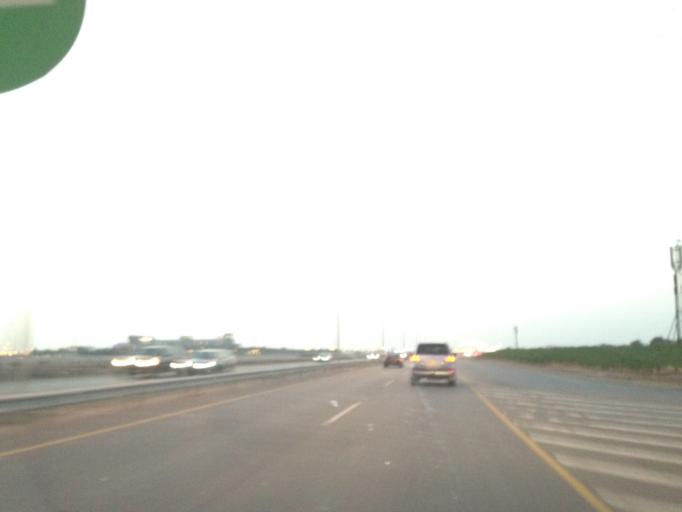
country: OM
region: Muhafazat Masqat
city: As Sib al Jadidah
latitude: 23.6206
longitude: 58.2731
